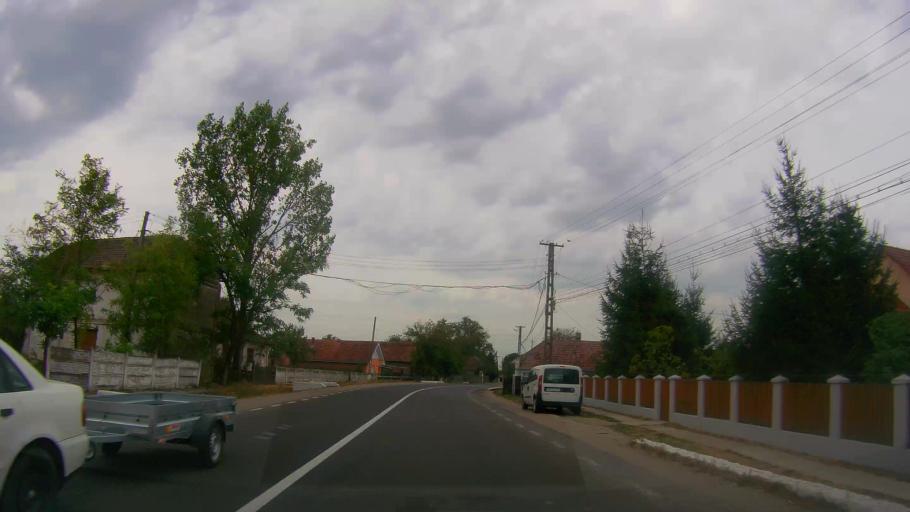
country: RO
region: Satu Mare
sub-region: Comuna Acas
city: Acas
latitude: 47.5407
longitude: 22.7856
